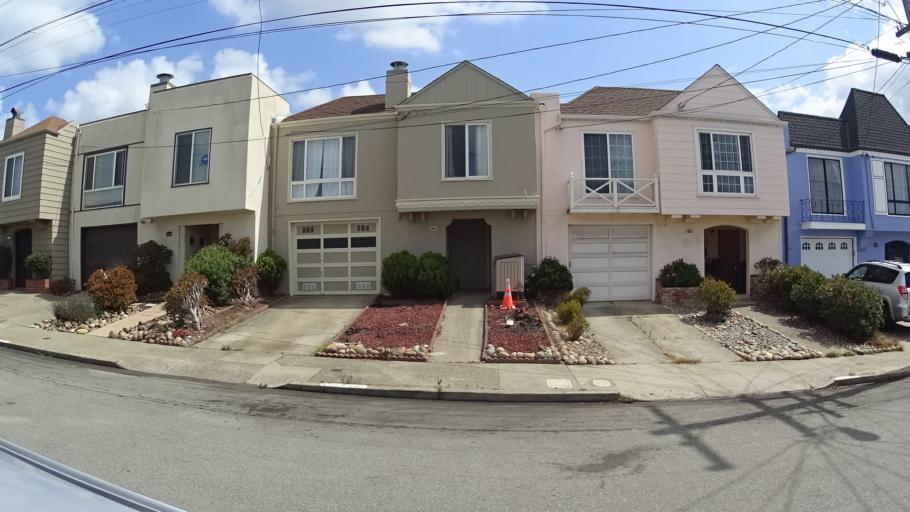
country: US
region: California
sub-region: San Mateo County
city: Daly City
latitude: 37.7359
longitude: -122.4978
